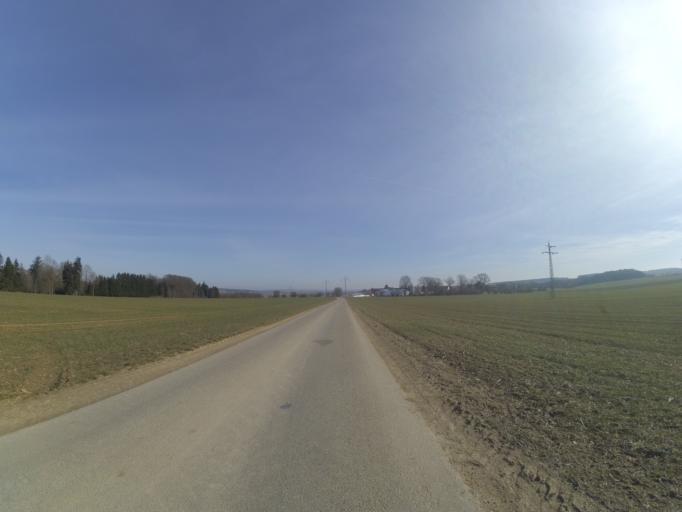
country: DE
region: Baden-Wuerttemberg
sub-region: Tuebingen Region
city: Beimerstetten
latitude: 48.4731
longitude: 10.0112
